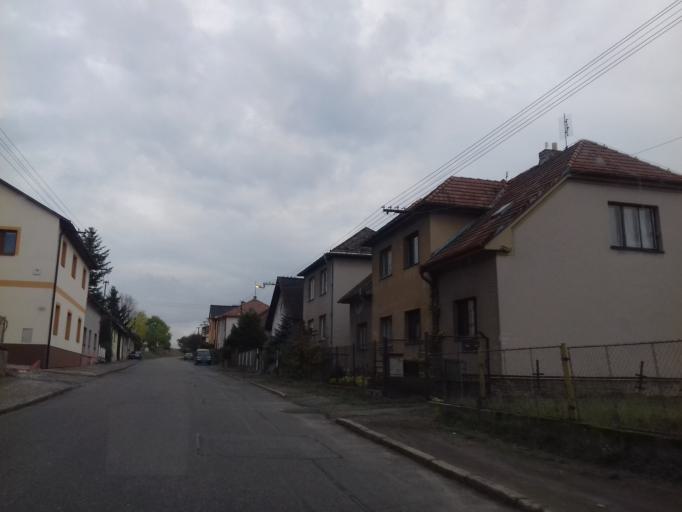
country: CZ
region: Pardubicky
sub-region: Okres Chrudim
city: Chrast
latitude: 49.9186
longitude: 15.9136
